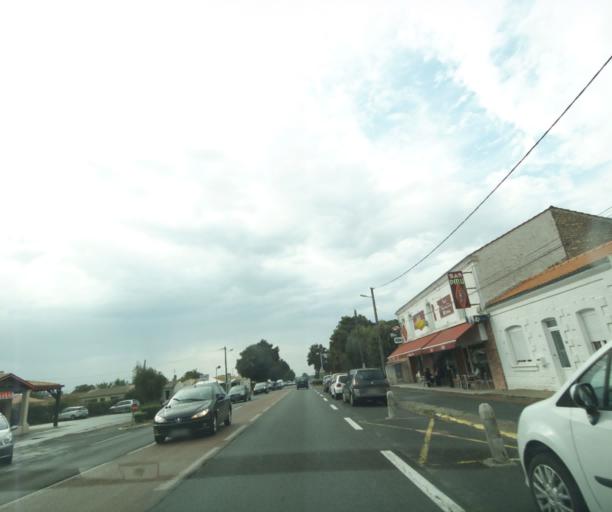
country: FR
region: Poitou-Charentes
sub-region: Departement de la Charente-Maritime
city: Tonnay-Charente
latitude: 45.9483
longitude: -0.9136
